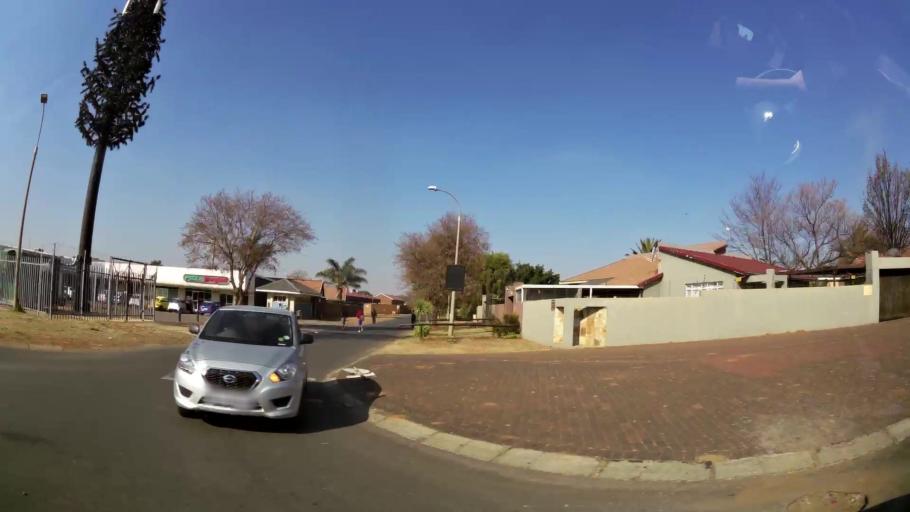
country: ZA
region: Gauteng
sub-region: West Rand District Municipality
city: Randfontein
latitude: -26.1802
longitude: 27.6835
